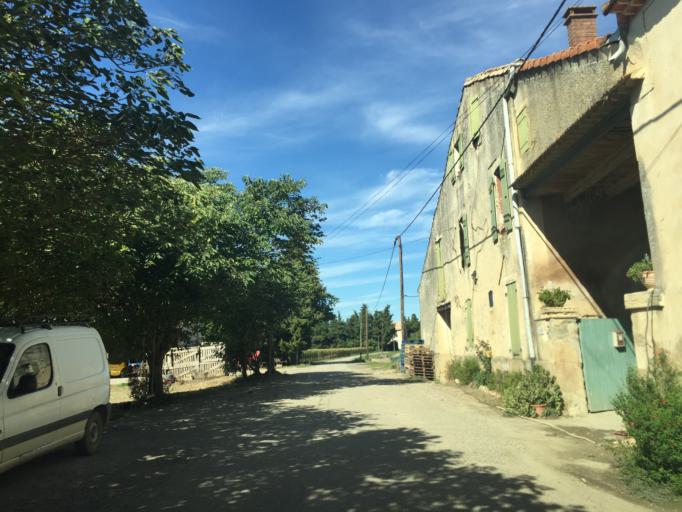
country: FR
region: Provence-Alpes-Cote d'Azur
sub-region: Departement du Vaucluse
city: Piolenc
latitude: 44.1710
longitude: 4.7363
